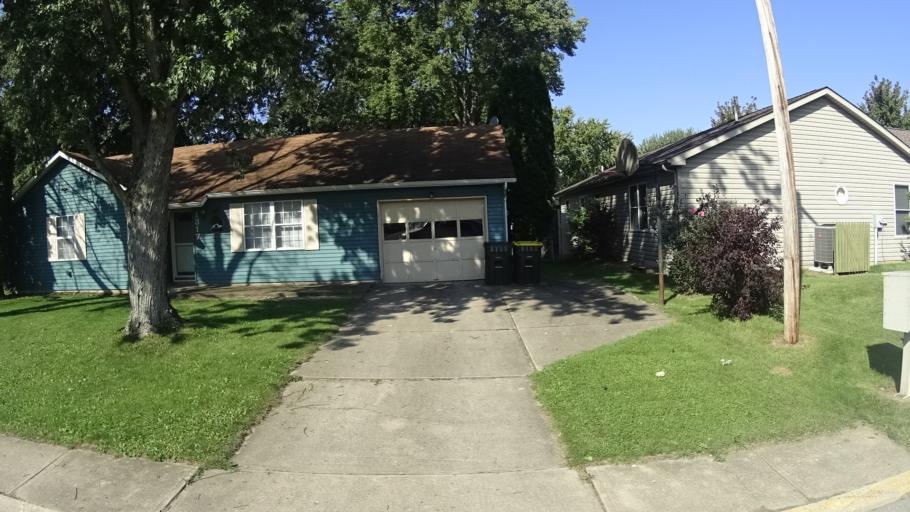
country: US
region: Indiana
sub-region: Madison County
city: Lapel
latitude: 40.0726
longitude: -85.8451
